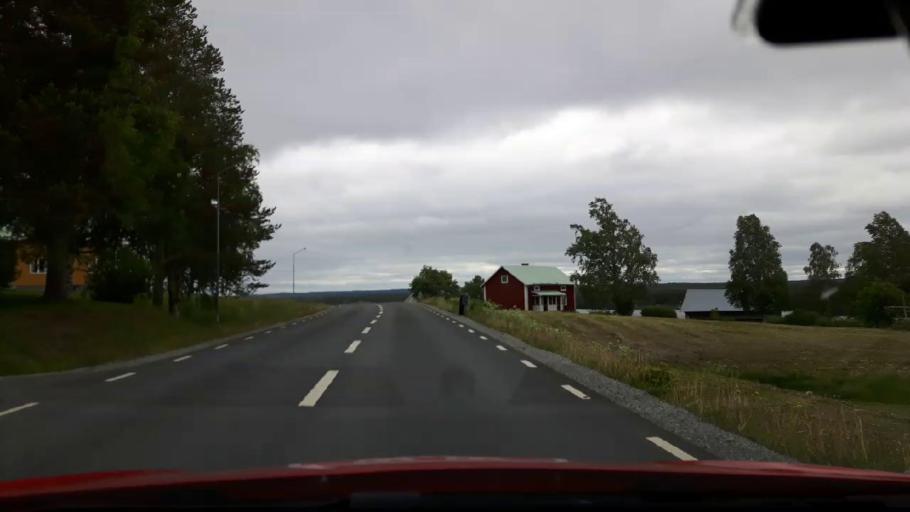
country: SE
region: Jaemtland
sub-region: OEstersunds Kommun
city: Lit
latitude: 63.7385
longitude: 14.8617
